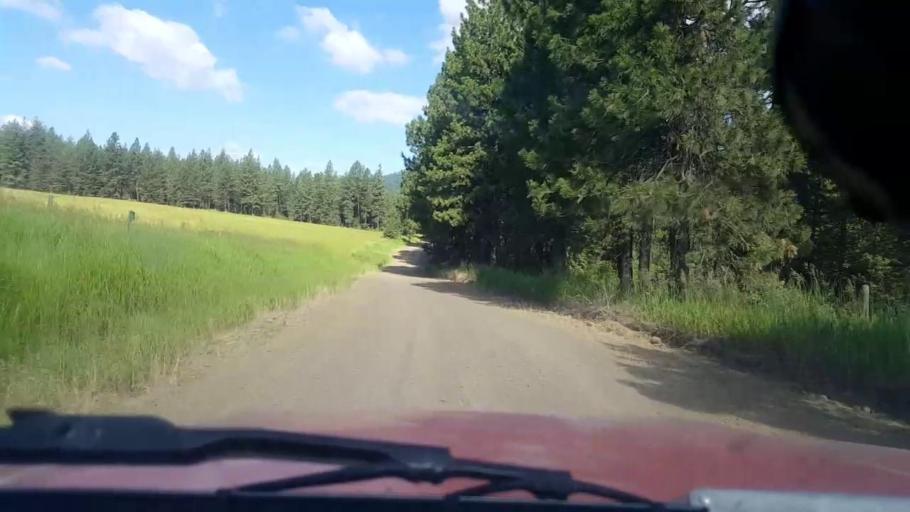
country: US
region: Washington
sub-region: Asotin County
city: Asotin
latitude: 46.0361
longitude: -117.4089
